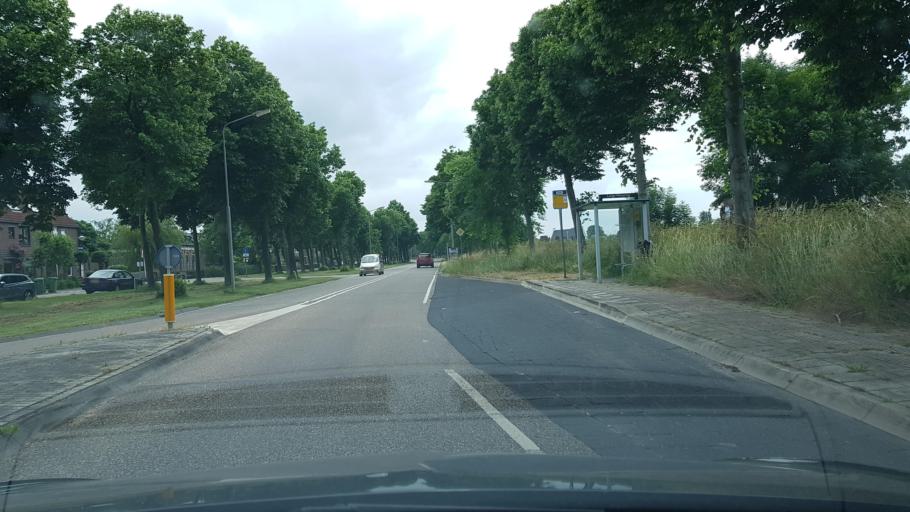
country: NL
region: Utrecht
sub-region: Stichtse Vecht
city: Vreeland
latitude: 52.2596
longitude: 5.0443
